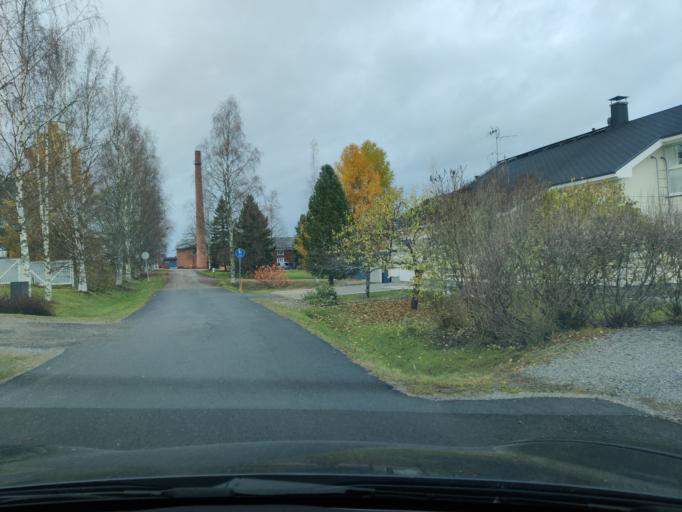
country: FI
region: Northern Savo
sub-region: Ylae-Savo
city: Kiuruvesi
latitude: 63.6510
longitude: 26.6345
